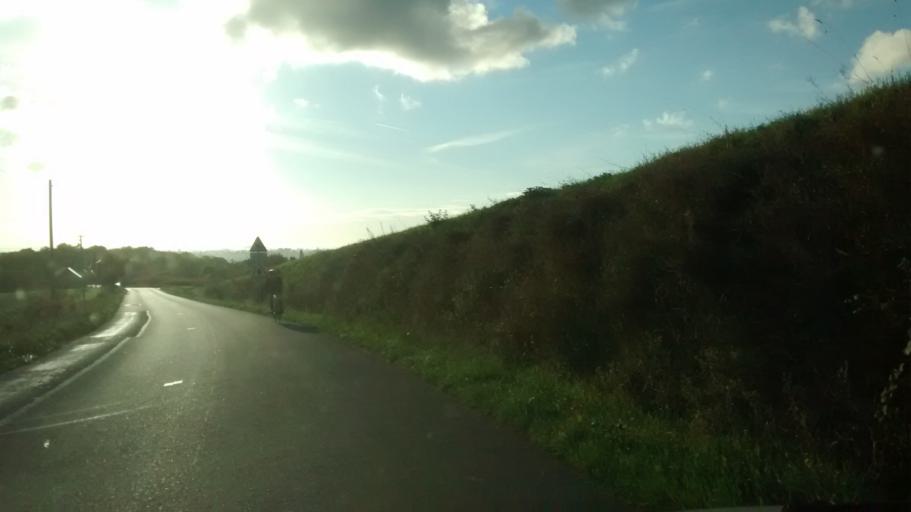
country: FR
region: Brittany
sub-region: Departement d'Ille-et-Vilaine
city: Saint-Meloir-des-Ondes
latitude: 48.6322
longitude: -1.8944
